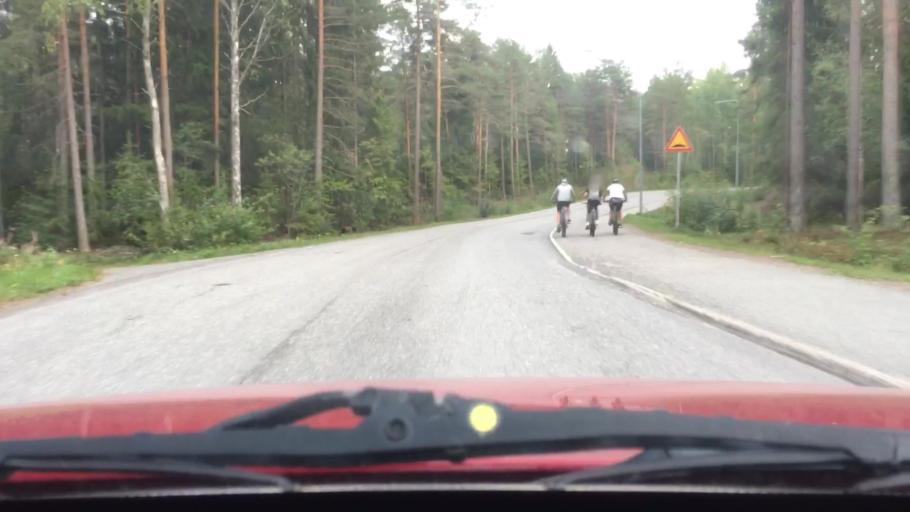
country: FI
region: Varsinais-Suomi
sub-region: Turku
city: Masku
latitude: 60.5530
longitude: 22.1332
